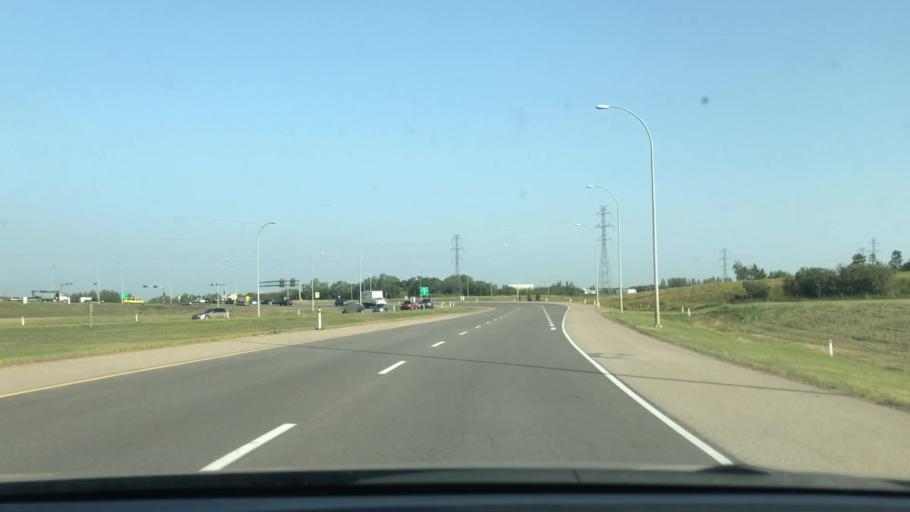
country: CA
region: Alberta
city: Beaumont
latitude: 53.4383
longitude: -113.4623
